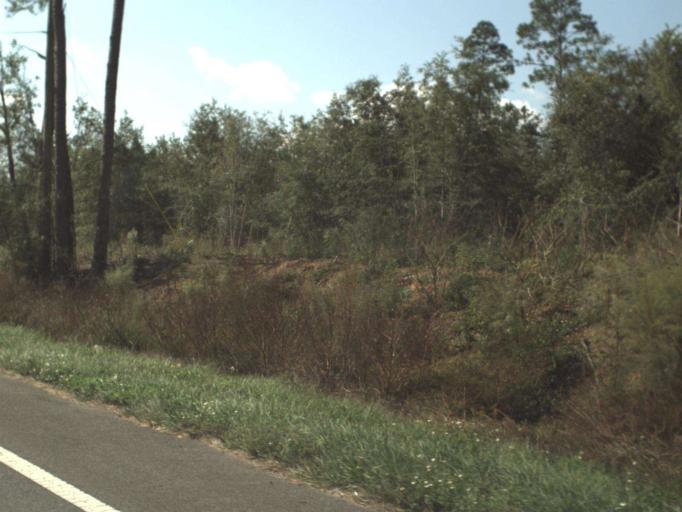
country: US
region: Florida
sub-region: Holmes County
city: Bonifay
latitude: 30.6000
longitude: -85.7658
